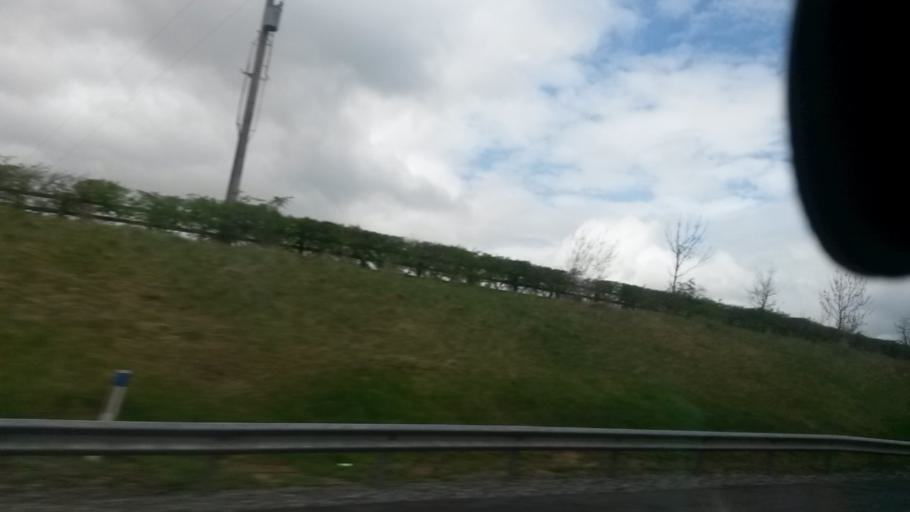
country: IE
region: Leinster
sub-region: Laois
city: Mountrath
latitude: 52.9036
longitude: -7.4886
